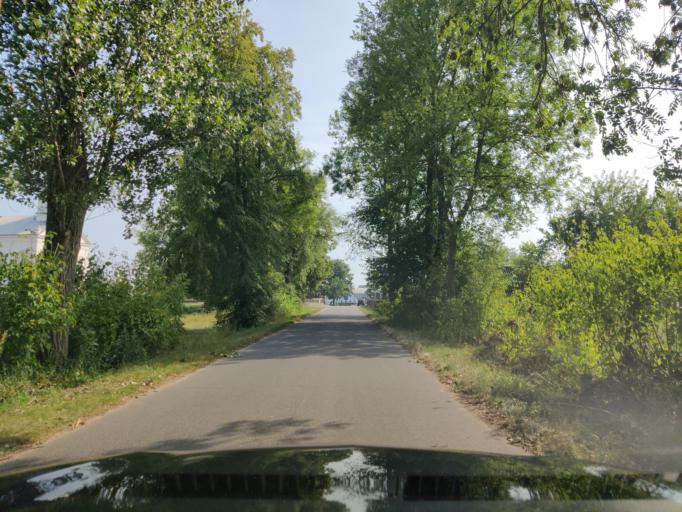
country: PL
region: Masovian Voivodeship
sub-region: Powiat pultuski
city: Obryte
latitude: 52.7586
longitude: 21.2172
